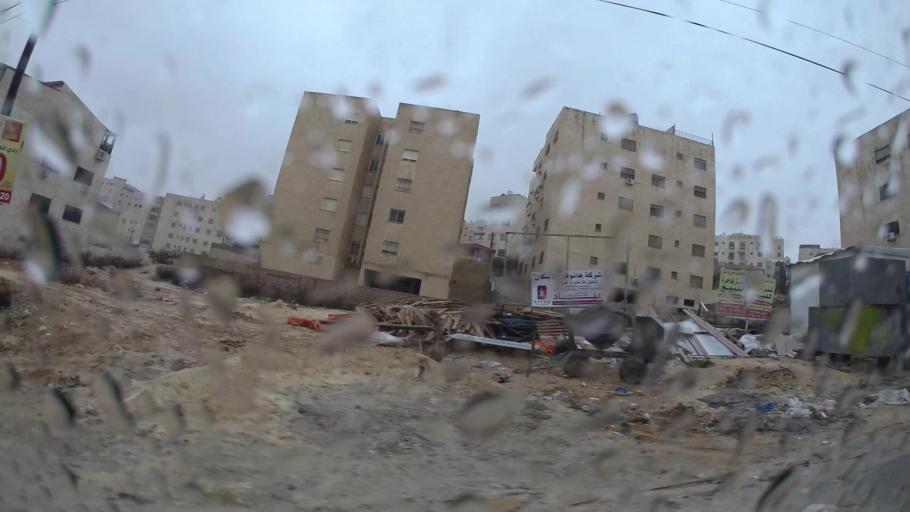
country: JO
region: Amman
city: Al Jubayhah
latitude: 32.0245
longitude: 35.8874
